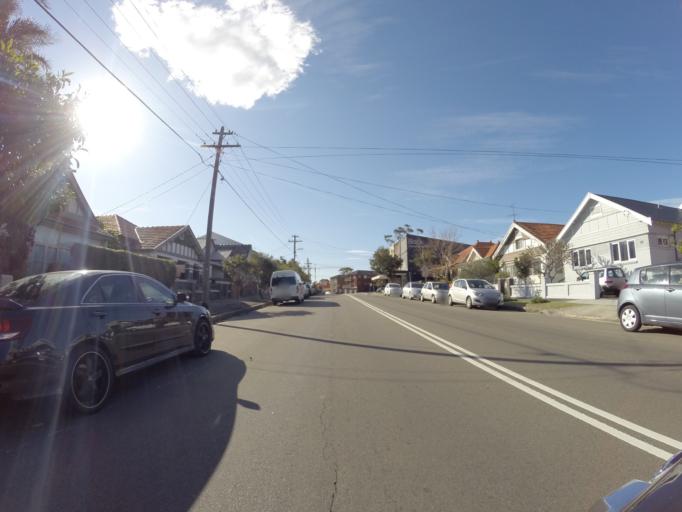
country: AU
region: New South Wales
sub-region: Randwick
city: Randwick
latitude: -33.9243
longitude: 151.2438
